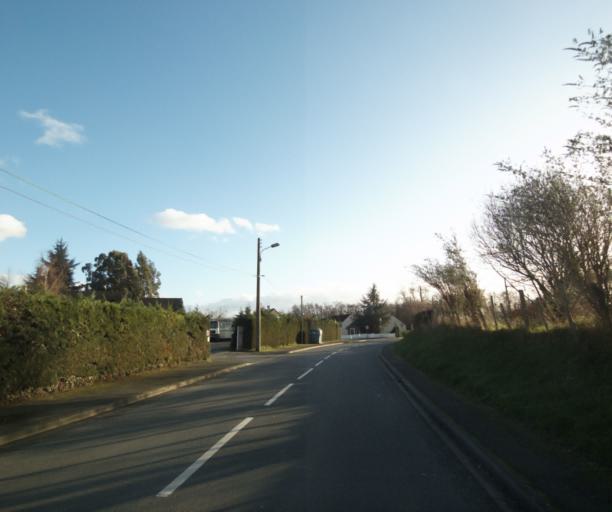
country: FR
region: Pays de la Loire
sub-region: Departement de la Sarthe
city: Allonnes
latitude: 47.9875
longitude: 0.1686
